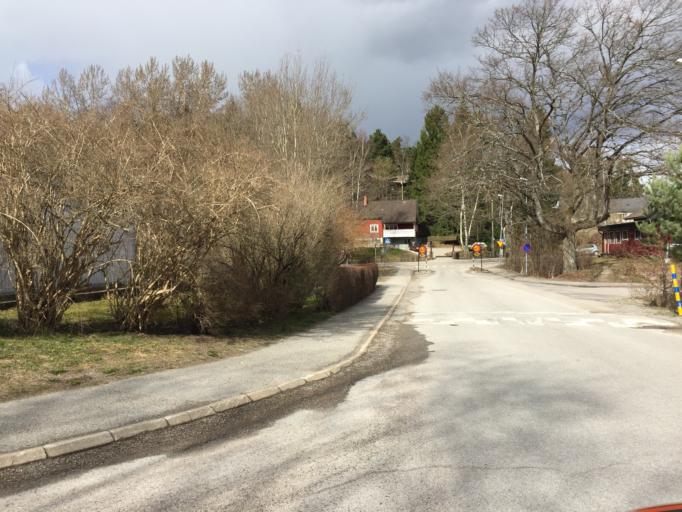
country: SE
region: Stockholm
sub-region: Botkyrka Kommun
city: Tumba
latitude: 59.1904
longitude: 17.8153
